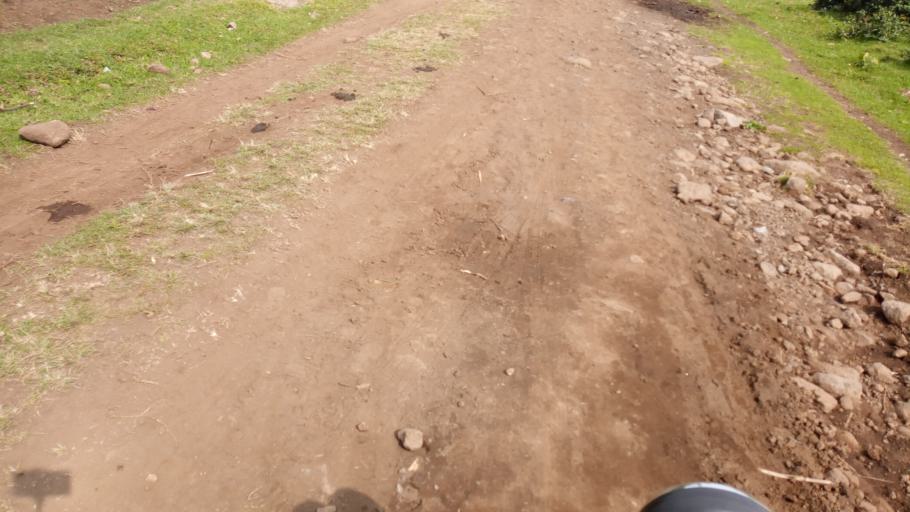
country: UG
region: Western Region
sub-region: Kisoro District
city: Kisoro
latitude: -1.3331
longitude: 29.6157
